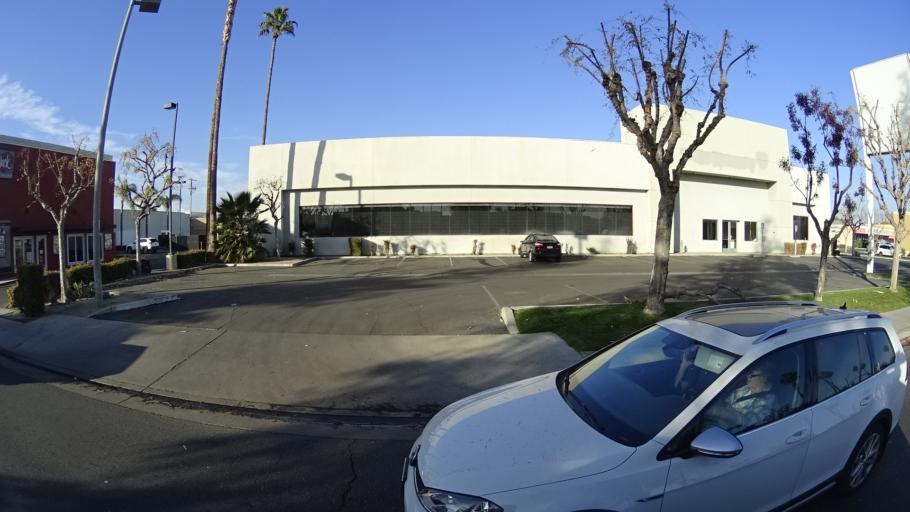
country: US
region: California
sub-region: Kern County
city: Bakersfield
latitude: 35.3395
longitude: -119.0352
